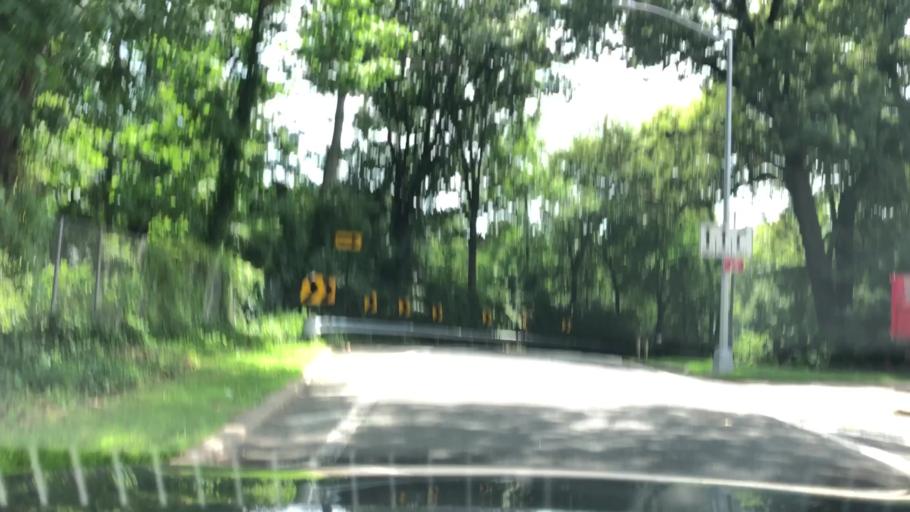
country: US
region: New York
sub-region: Queens County
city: Jamaica
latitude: 40.7208
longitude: -73.7810
